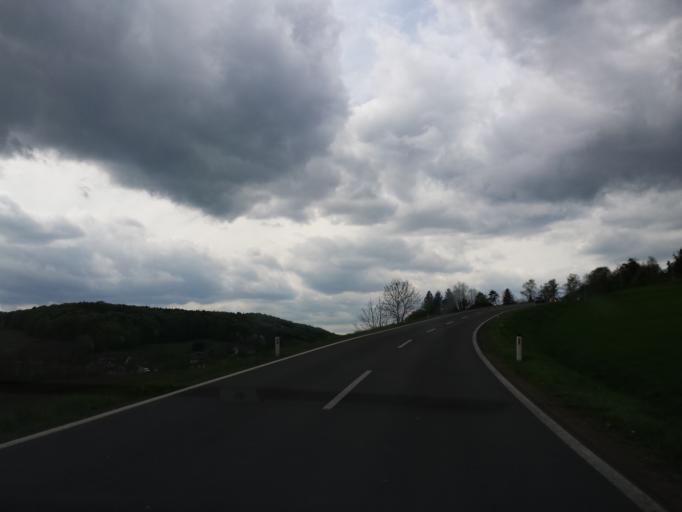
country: AT
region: Styria
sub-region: Politischer Bezirk Suedoststeiermark
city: Riegersburg
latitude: 46.9973
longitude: 15.9378
